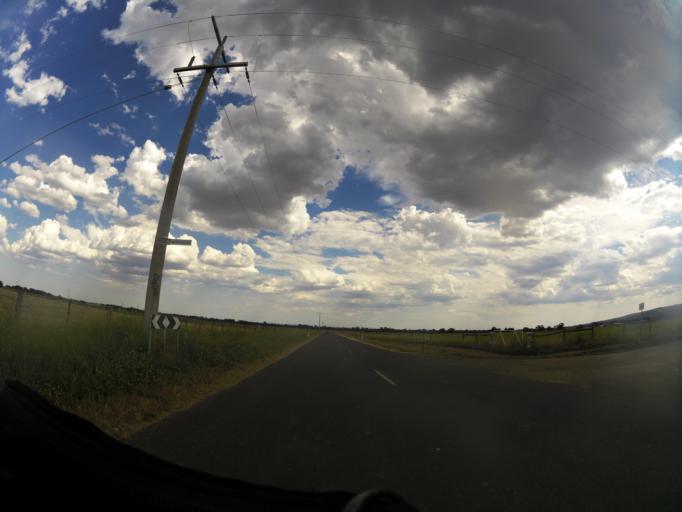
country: AU
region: Victoria
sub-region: Wellington
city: Heyfield
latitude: -37.9913
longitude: 146.6928
